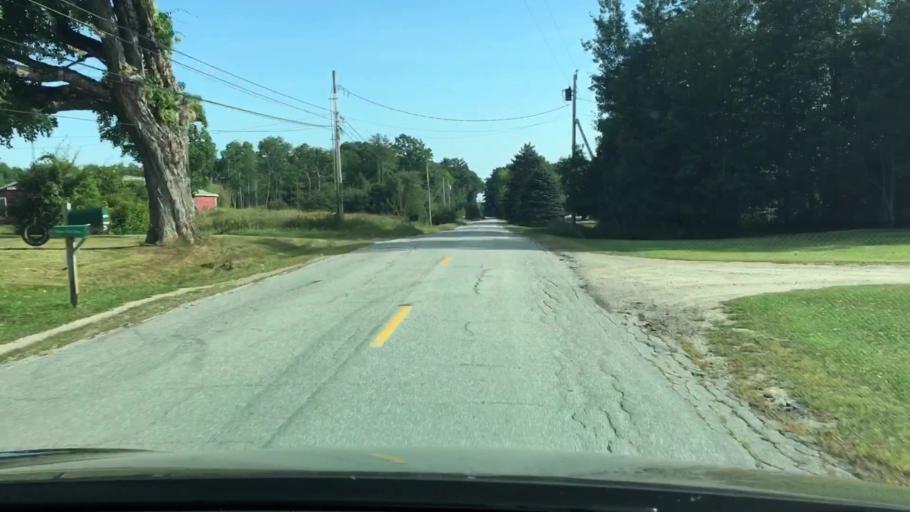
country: US
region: Maine
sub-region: Hancock County
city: Bucksport
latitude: 44.5431
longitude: -68.7961
